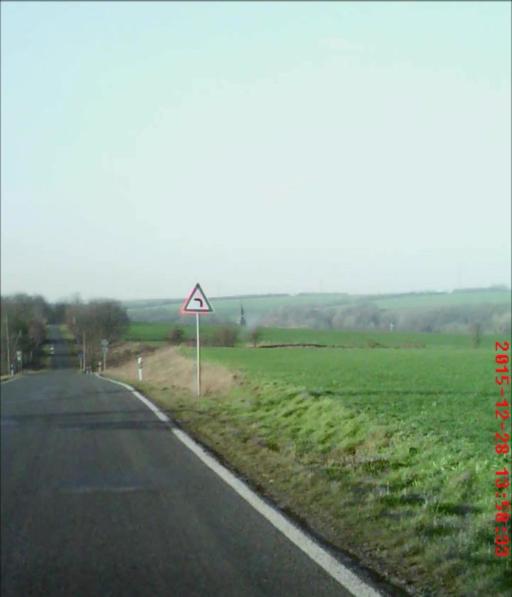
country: DE
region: Thuringia
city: Eberstedt
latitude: 51.0671
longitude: 11.5964
